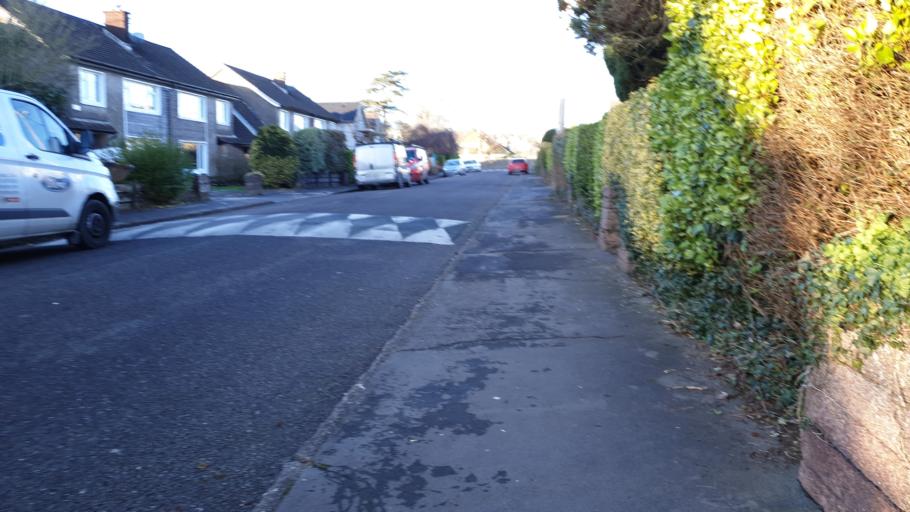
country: IE
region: Munster
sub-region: County Cork
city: Cork
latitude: 51.8927
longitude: -8.4451
